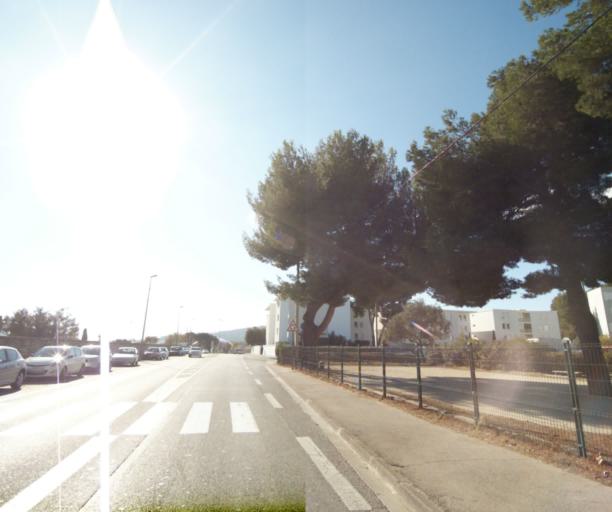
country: FR
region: Provence-Alpes-Cote d'Azur
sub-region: Departement des Bouches-du-Rhone
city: La Ciotat
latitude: 43.1937
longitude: 5.6104
